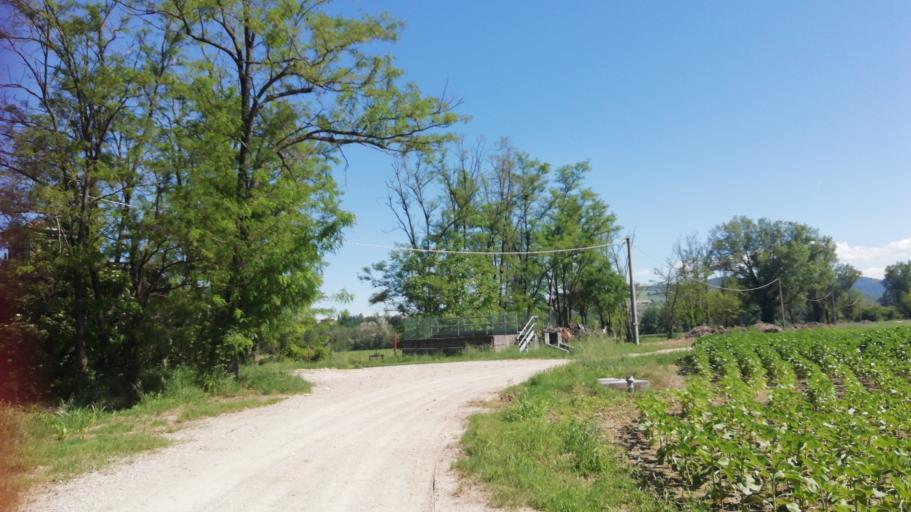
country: IT
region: Emilia-Romagna
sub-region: Provincia di Piacenza
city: Borgonovo Valtidone
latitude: 44.9856
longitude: 9.4592
